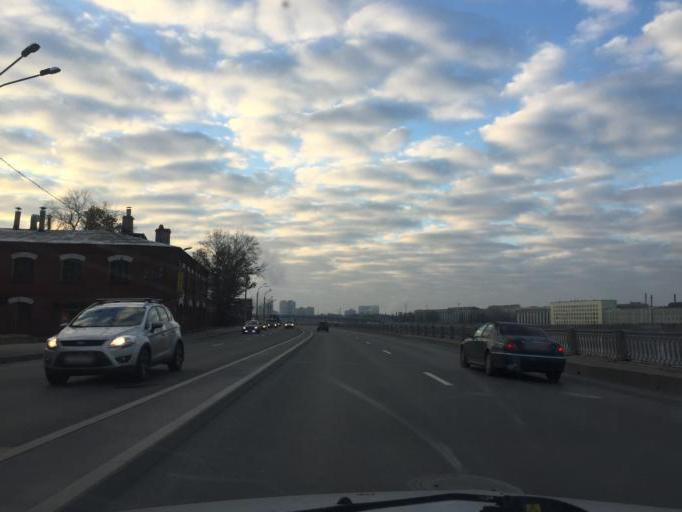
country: RU
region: St.-Petersburg
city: Obukhovo
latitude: 59.8864
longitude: 30.4490
